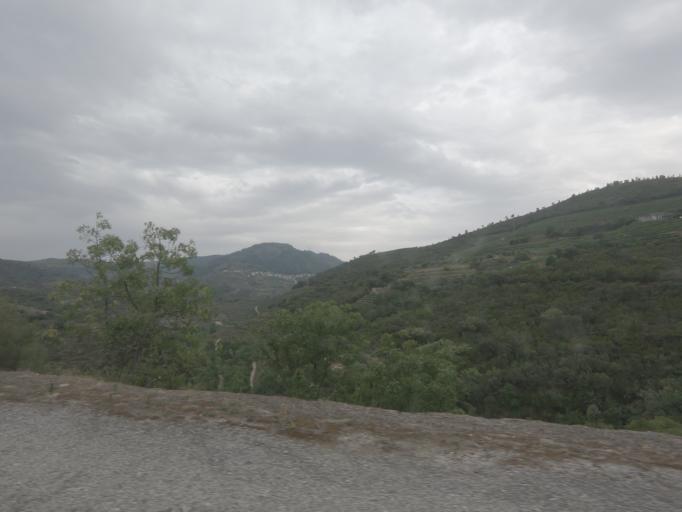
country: PT
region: Viseu
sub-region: Armamar
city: Armamar
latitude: 41.1390
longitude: -7.6433
